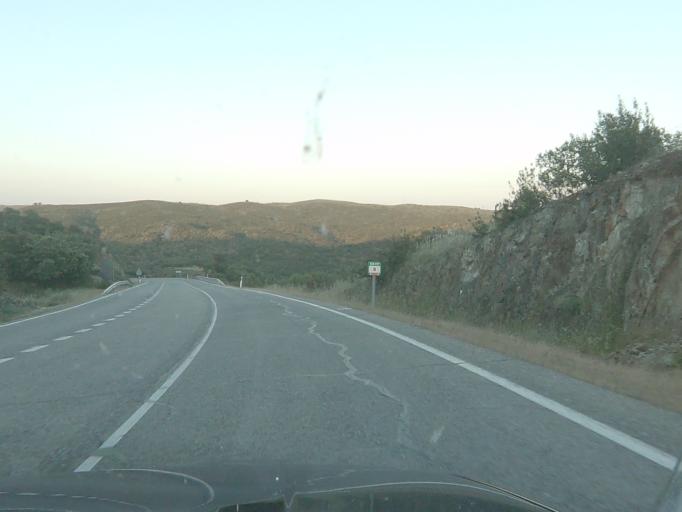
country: ES
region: Extremadura
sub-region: Provincia de Caceres
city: Salorino
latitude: 39.5671
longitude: -7.0027
